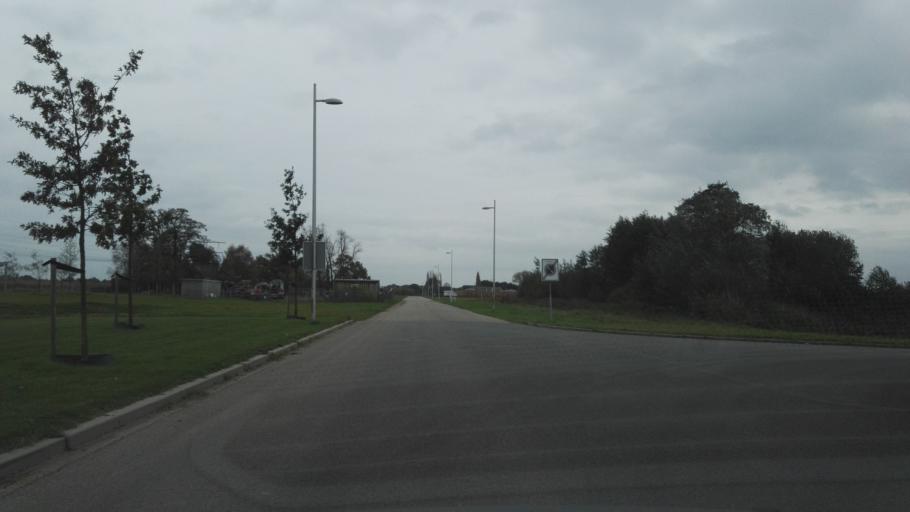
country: NL
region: Gelderland
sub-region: Gemeente Apeldoorn
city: Apeldoorn
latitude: 52.2452
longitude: 6.0047
